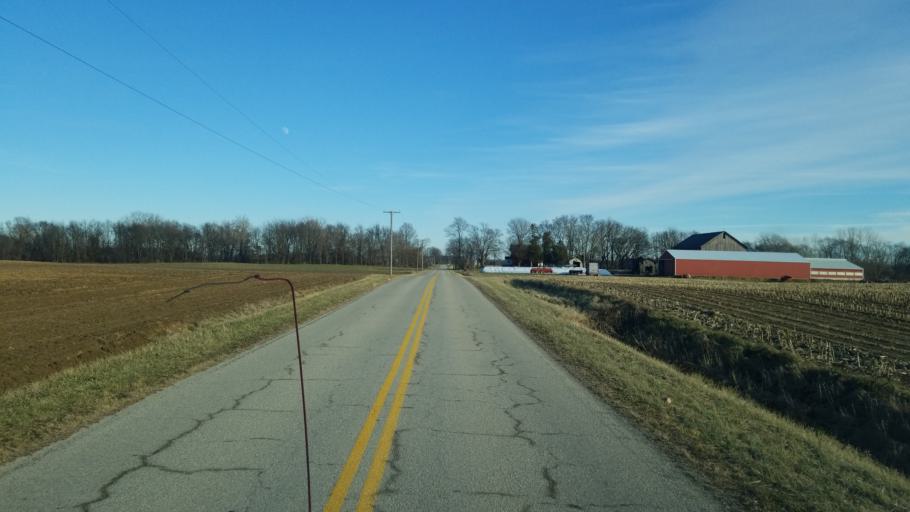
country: US
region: Ohio
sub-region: Huron County
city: Monroeville
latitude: 41.1755
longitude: -82.6941
